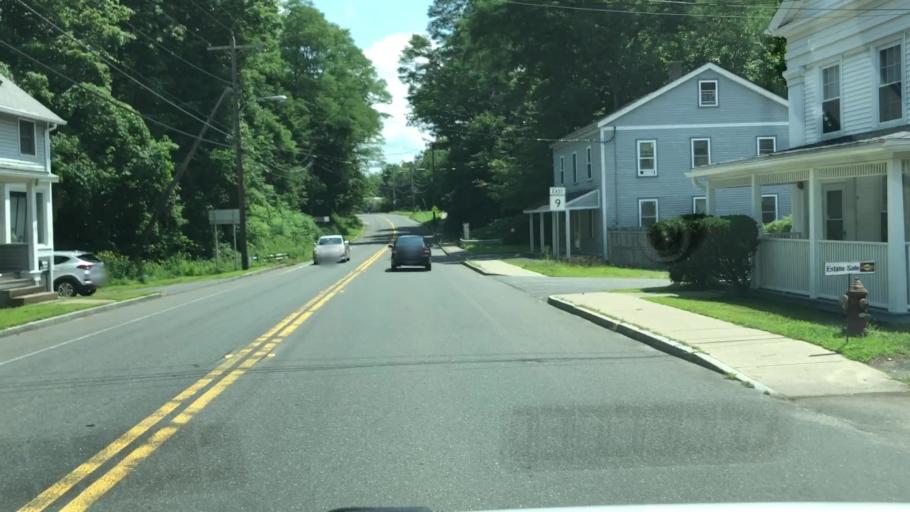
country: US
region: Massachusetts
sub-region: Hampshire County
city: Williamsburg
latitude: 42.3741
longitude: -72.7013
